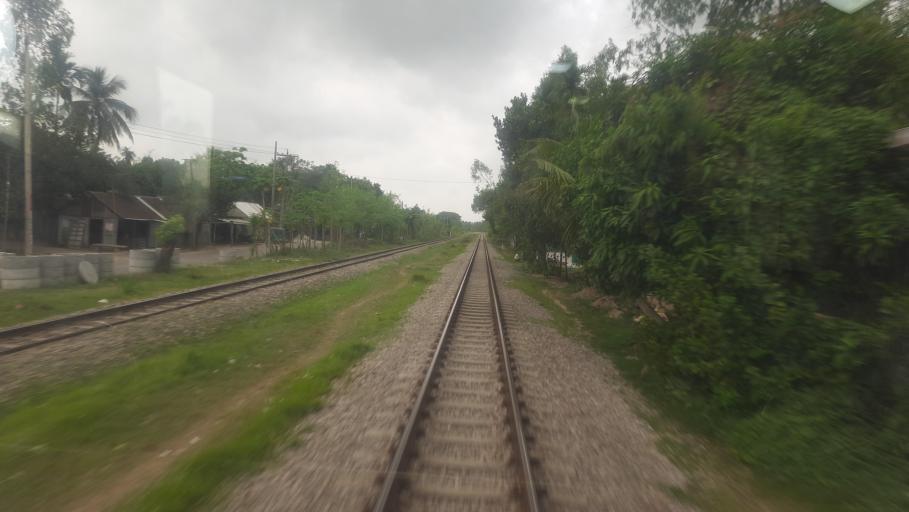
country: BD
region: Dhaka
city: Narsingdi
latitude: 23.9657
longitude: 90.8172
